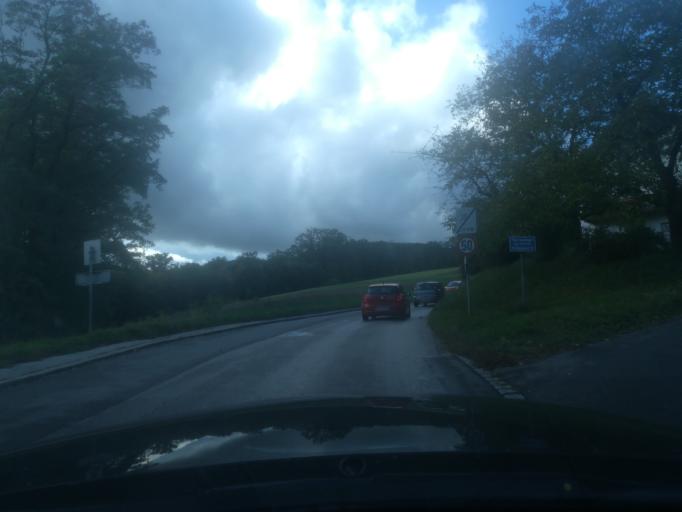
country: AT
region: Upper Austria
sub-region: Linz Stadt
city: Linz
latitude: 48.3353
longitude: 14.2788
